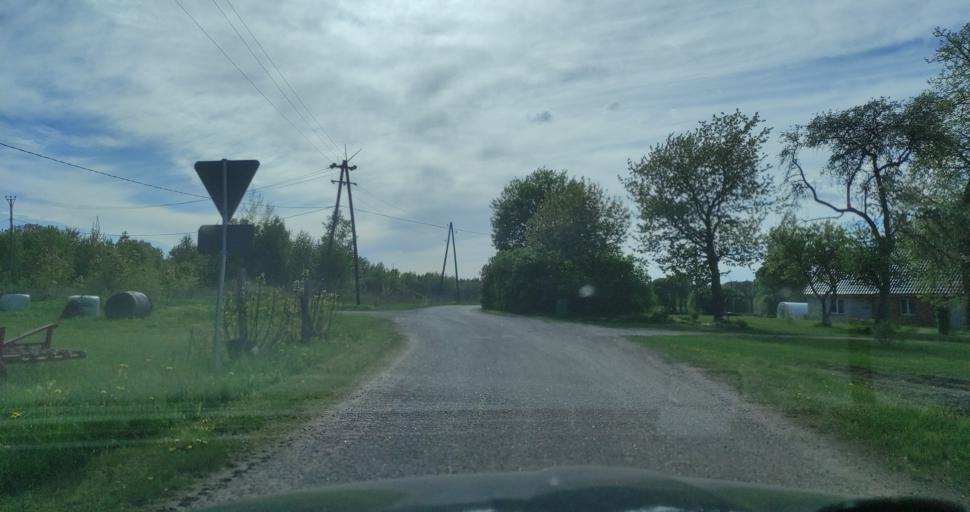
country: LV
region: Kuldigas Rajons
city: Kuldiga
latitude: 56.9177
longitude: 21.8978
